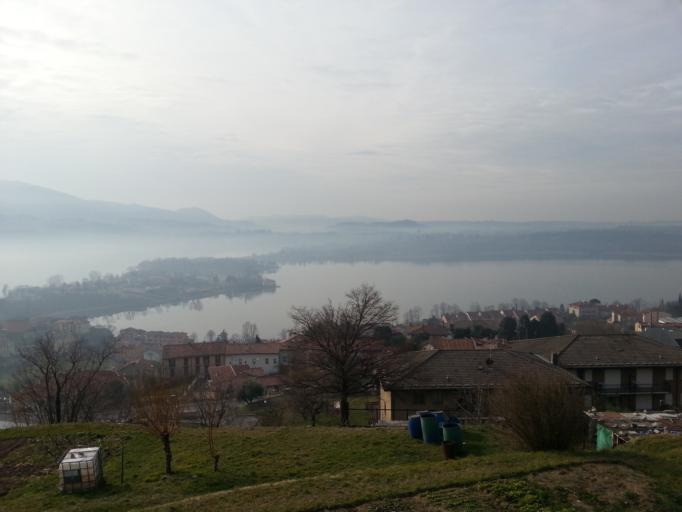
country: IT
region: Lombardy
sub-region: Provincia di Lecco
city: Civate
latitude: 45.8292
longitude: 9.3389
